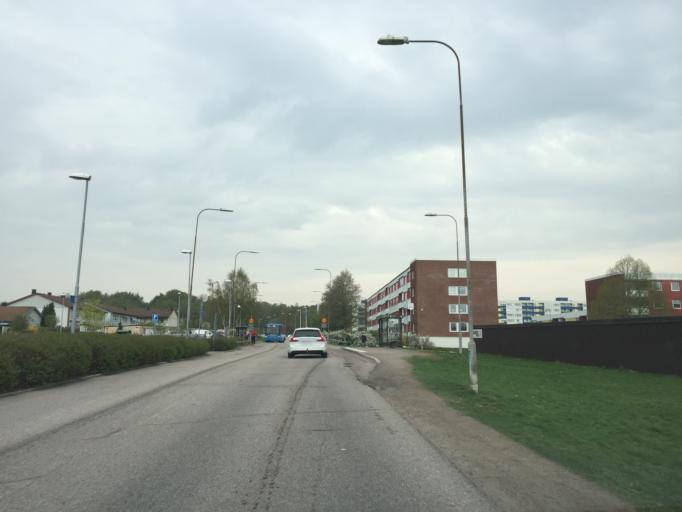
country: SE
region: Vaestra Goetaland
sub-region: Ale Kommun
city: Surte
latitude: 57.7955
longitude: 11.9907
